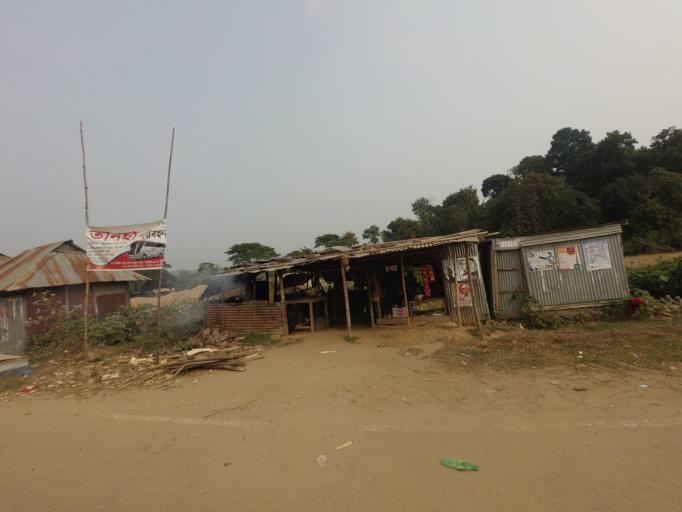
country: BD
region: Dhaka
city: Netrakona
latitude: 25.1735
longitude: 90.6563
